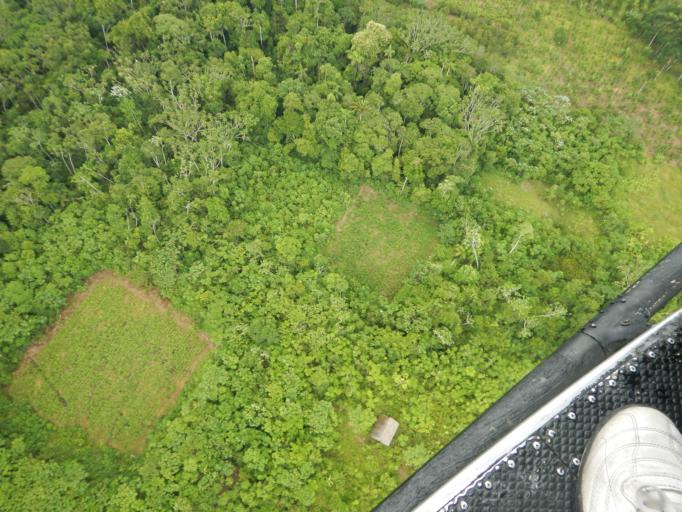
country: BO
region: Cochabamba
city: Chimore
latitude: -17.1404
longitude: -64.7041
